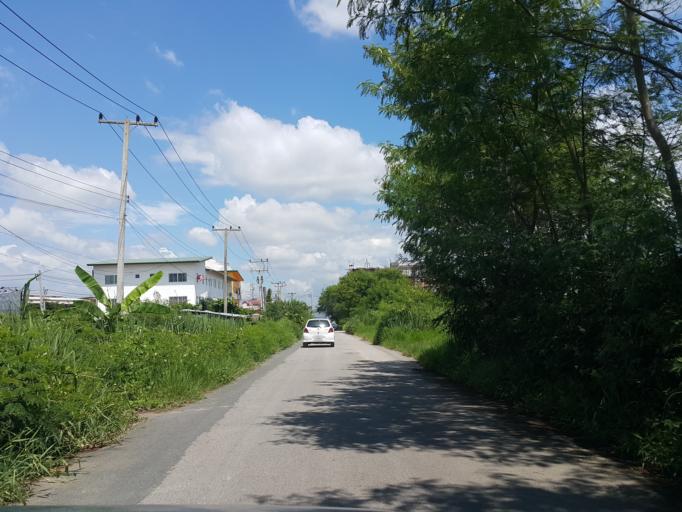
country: TH
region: Chiang Mai
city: Chiang Mai
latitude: 18.7407
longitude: 98.9618
